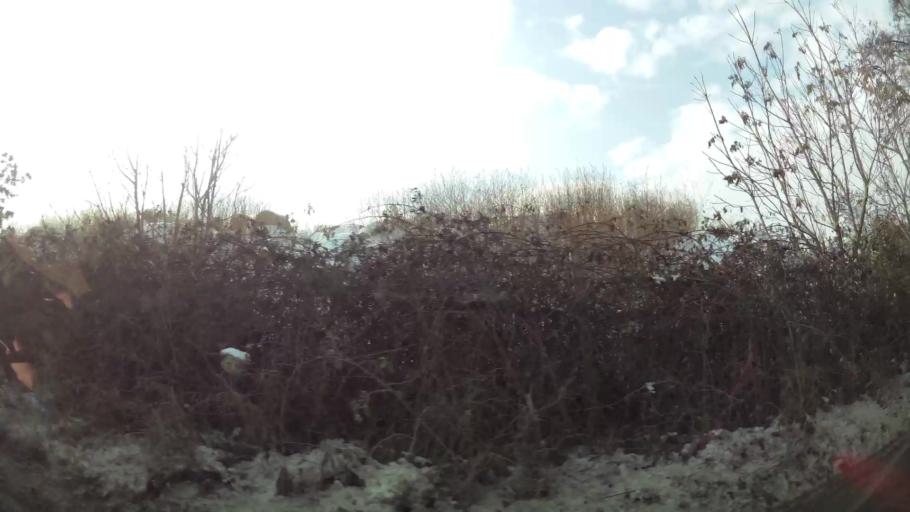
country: MK
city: Krushopek
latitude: 42.0143
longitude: 21.3711
